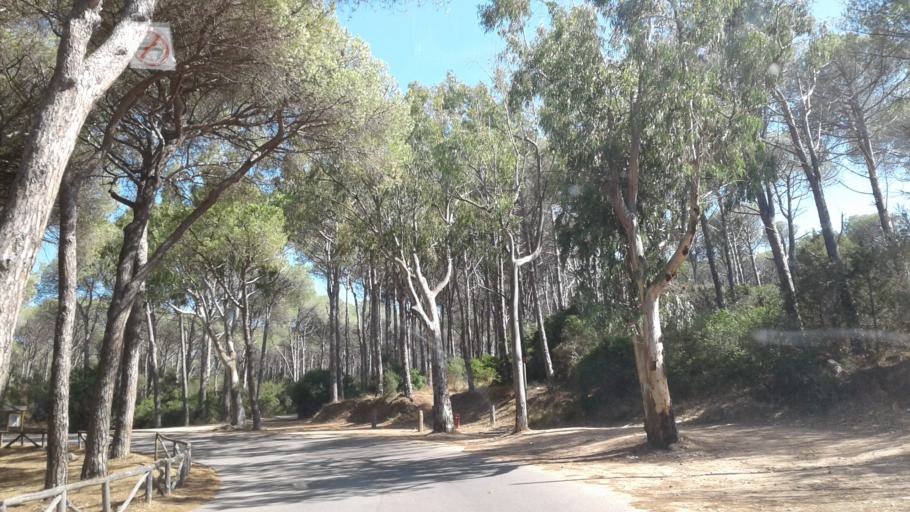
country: IT
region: Sardinia
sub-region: Provincia di Olbia-Tempio
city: La Maddalena
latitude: 41.2109
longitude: 9.4557
